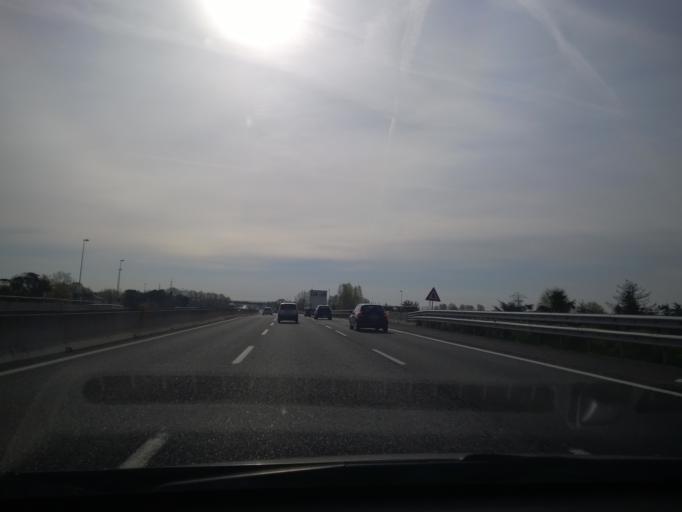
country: IT
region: Emilia-Romagna
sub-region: Forli-Cesena
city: Forli
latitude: 44.2516
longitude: 12.0923
